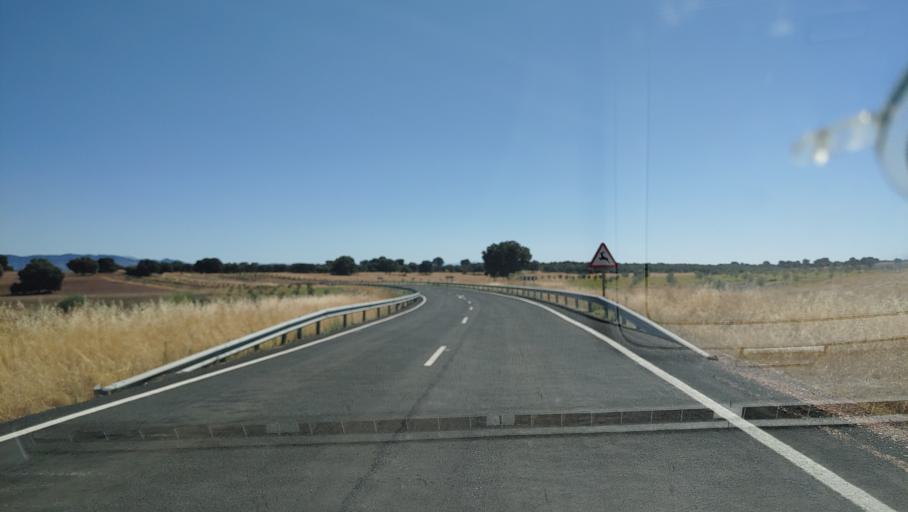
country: ES
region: Castille-La Mancha
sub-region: Provincia de Ciudad Real
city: Albaladejo
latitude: 38.5427
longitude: -2.7881
